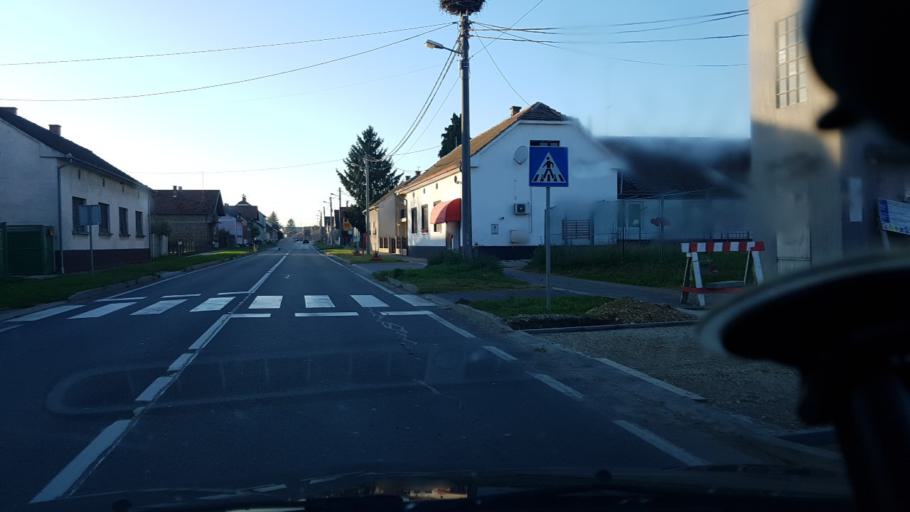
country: HR
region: Koprivnicko-Krizevacka
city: Virje
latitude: 46.0625
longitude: 16.9973
